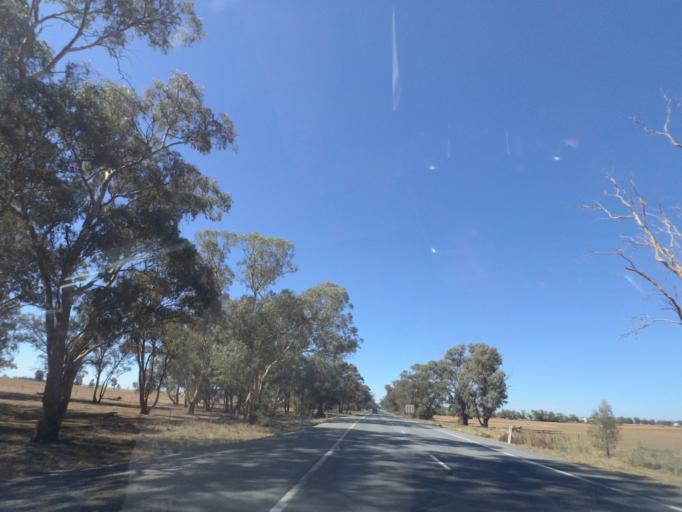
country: AU
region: New South Wales
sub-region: Bland
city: West Wyalong
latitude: -34.2036
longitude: 147.1099
